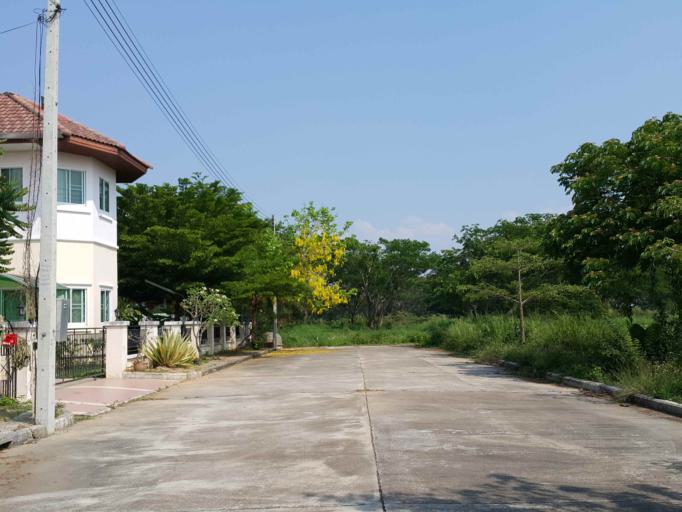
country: TH
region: Chiang Mai
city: Saraphi
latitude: 18.7522
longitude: 99.0437
